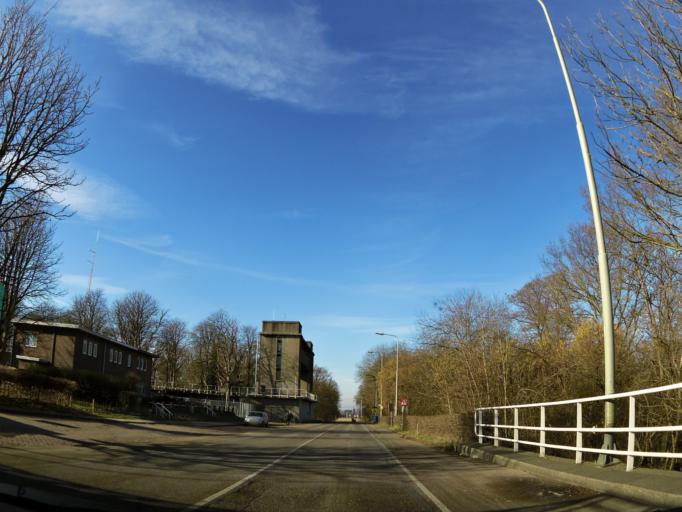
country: NL
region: Limburg
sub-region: Gemeente Sittard-Geleen
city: Born
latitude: 51.0363
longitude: 5.7989
